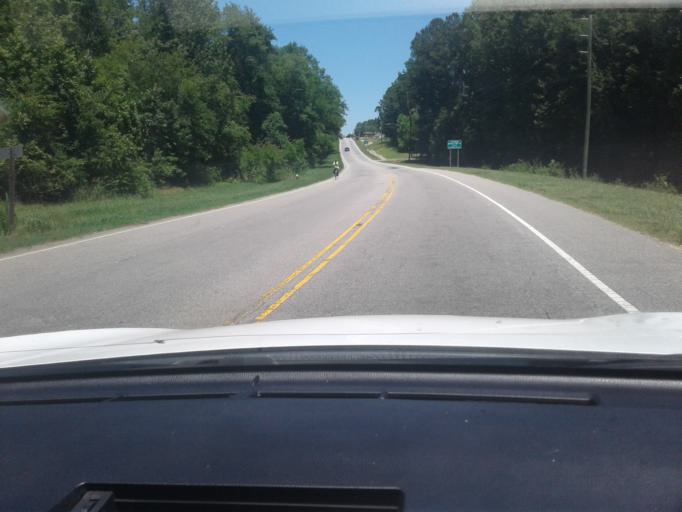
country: US
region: North Carolina
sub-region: Harnett County
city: Erwin
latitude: 35.3126
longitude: -78.6899
